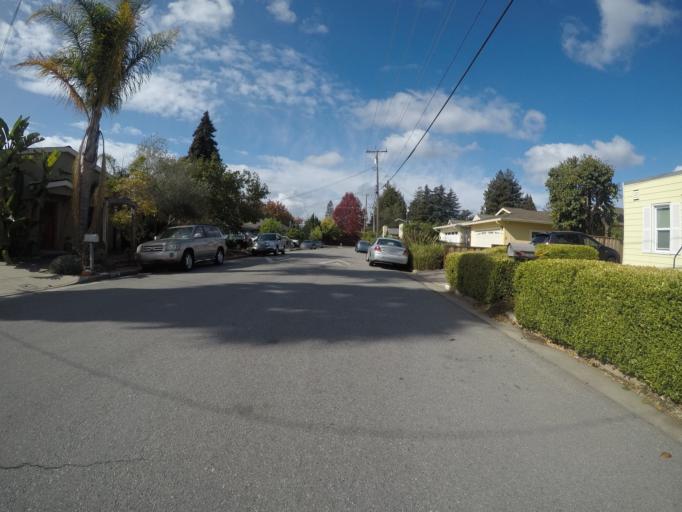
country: US
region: California
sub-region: Santa Cruz County
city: Twin Lakes
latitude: 36.9855
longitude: -121.9991
